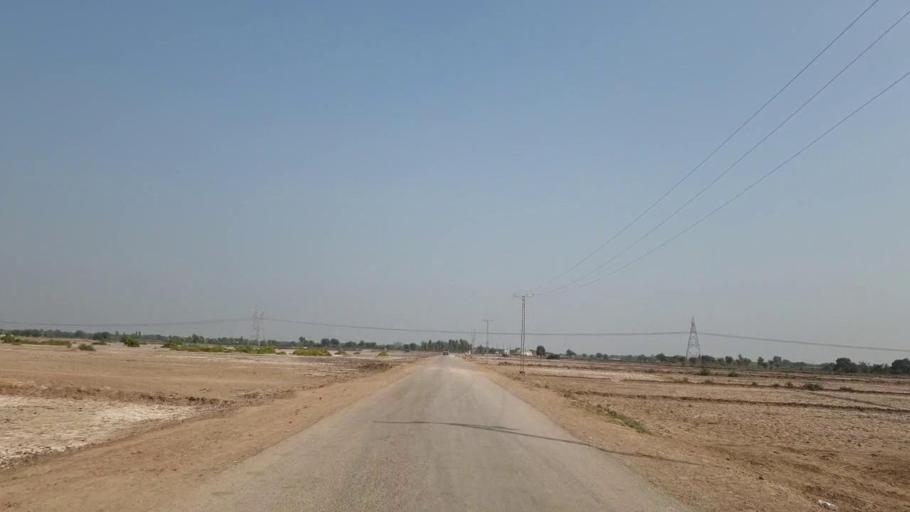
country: PK
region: Sindh
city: Matiari
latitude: 25.5019
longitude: 68.4505
